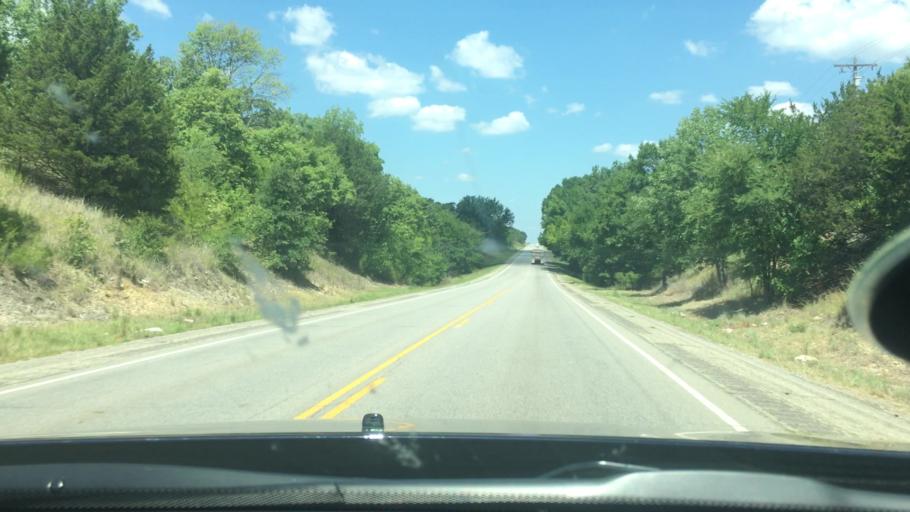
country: US
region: Oklahoma
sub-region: Marshall County
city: Oakland
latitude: 34.1483
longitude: -96.8106
